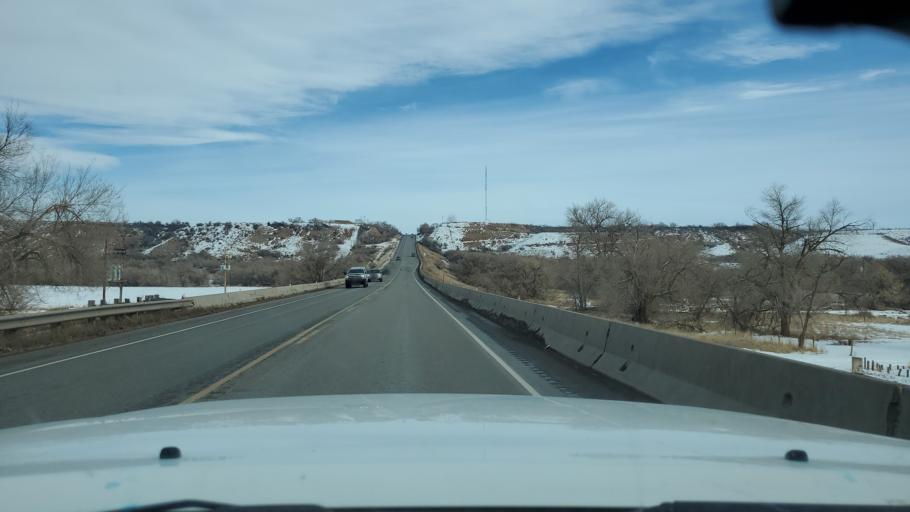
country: US
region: Utah
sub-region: Duchesne County
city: Roosevelt
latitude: 40.3020
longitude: -109.9130
